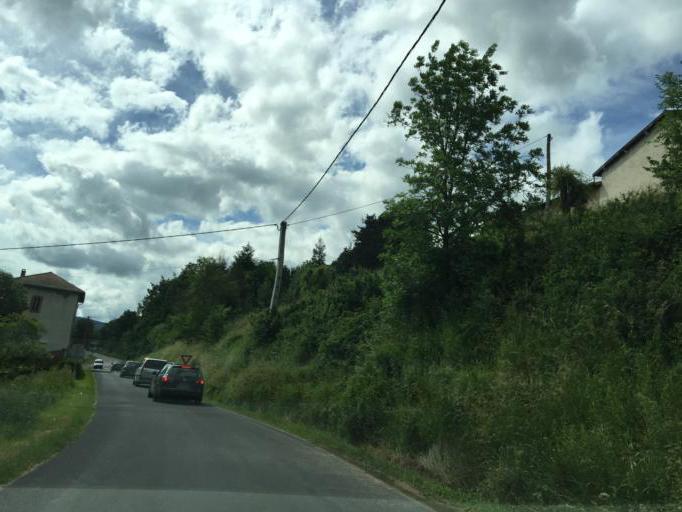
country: FR
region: Auvergne
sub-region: Departement du Puy-de-Dome
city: Ambert
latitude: 45.5432
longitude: 3.7589
